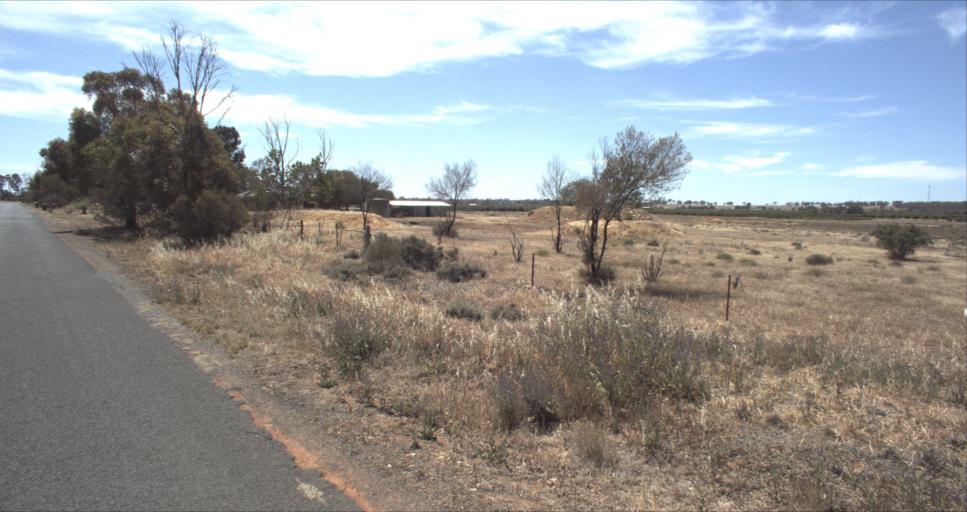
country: AU
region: New South Wales
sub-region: Leeton
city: Leeton
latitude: -34.5973
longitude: 146.4277
